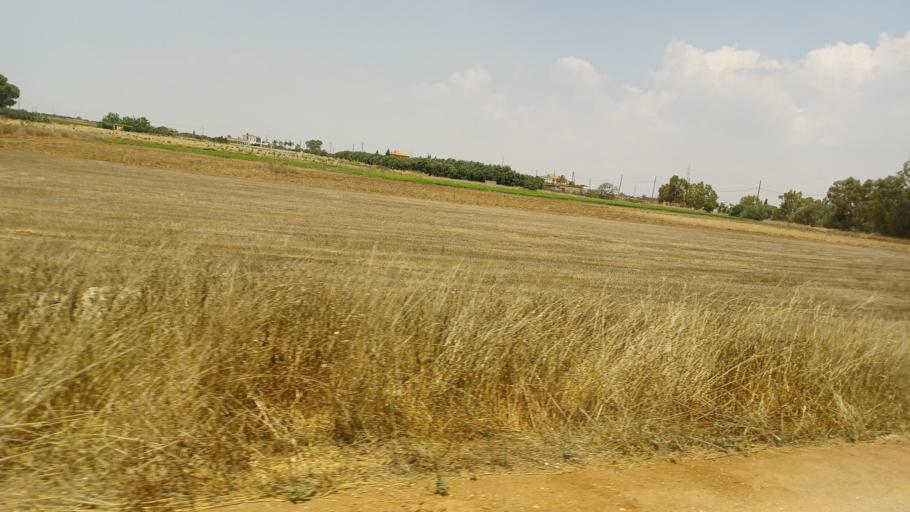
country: CY
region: Ammochostos
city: Liopetri
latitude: 34.9927
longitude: 33.8518
